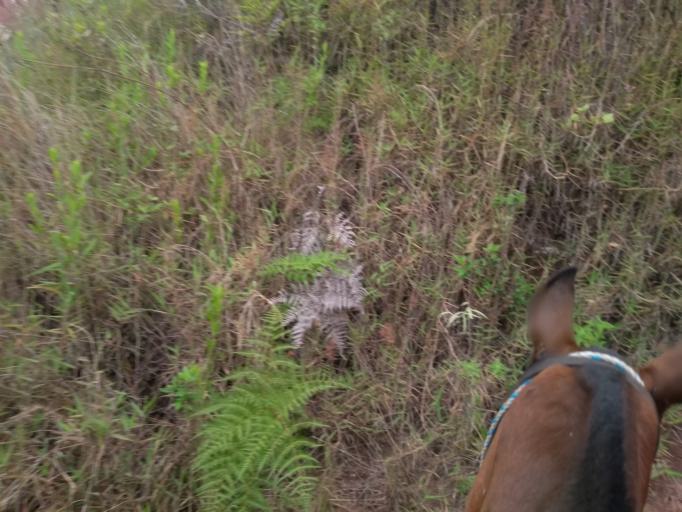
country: CO
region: Cesar
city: San Diego
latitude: 10.1791
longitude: -73.0381
